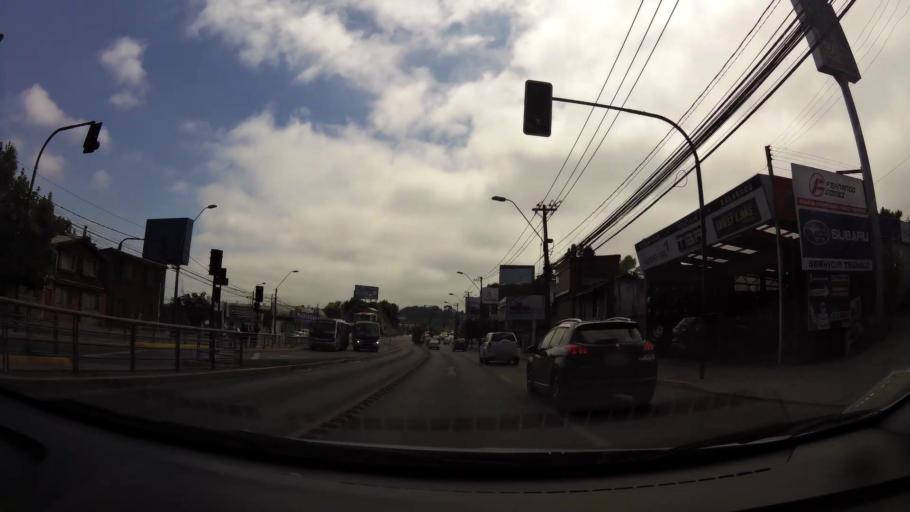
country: CL
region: Biobio
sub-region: Provincia de Concepcion
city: Concepcion
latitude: -36.8052
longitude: -73.0539
